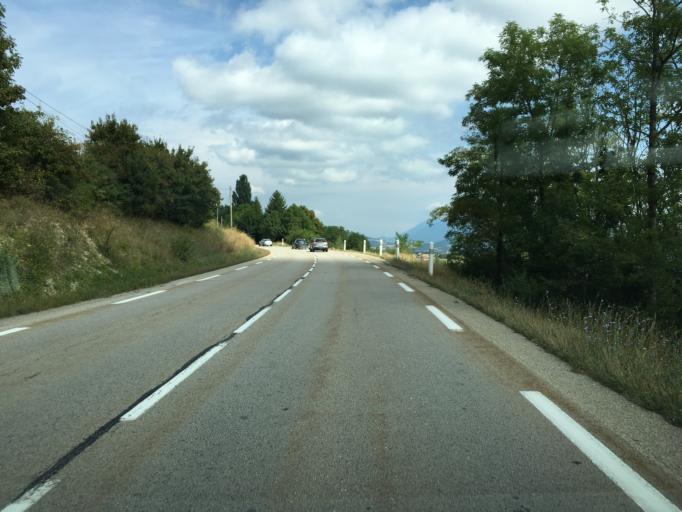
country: FR
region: Rhone-Alpes
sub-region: Departement de l'Isere
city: Mens
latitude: 44.7777
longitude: 5.6529
